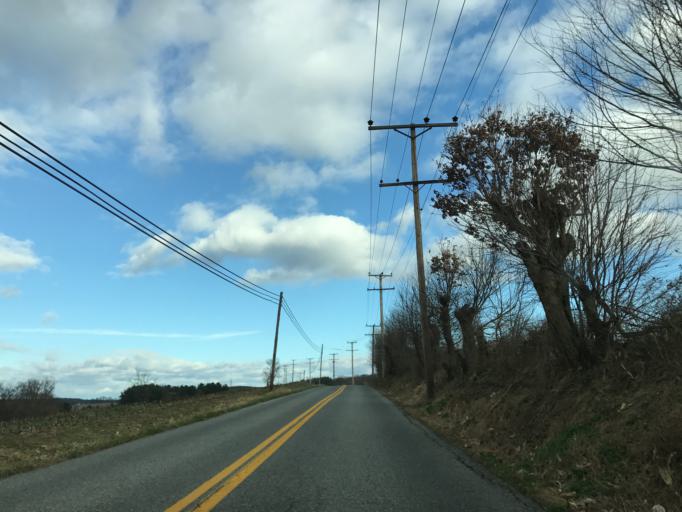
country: US
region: Maryland
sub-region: Harford County
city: Jarrettsville
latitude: 39.6371
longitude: -76.5875
